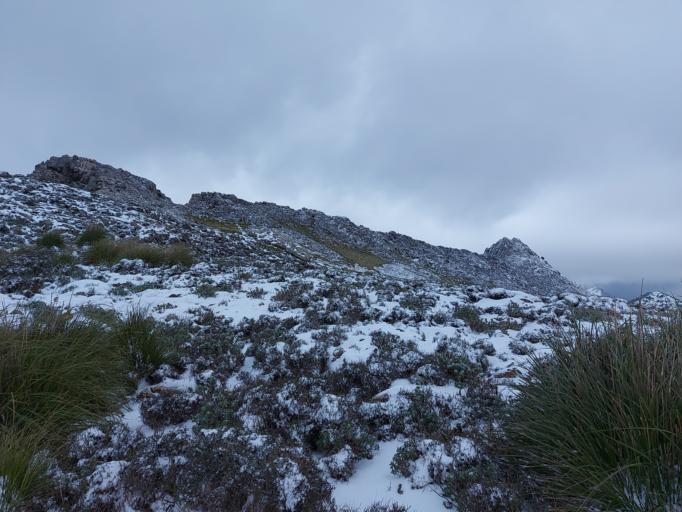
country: ES
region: Balearic Islands
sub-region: Illes Balears
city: Fornalutx
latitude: 39.7741
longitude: 2.7604
